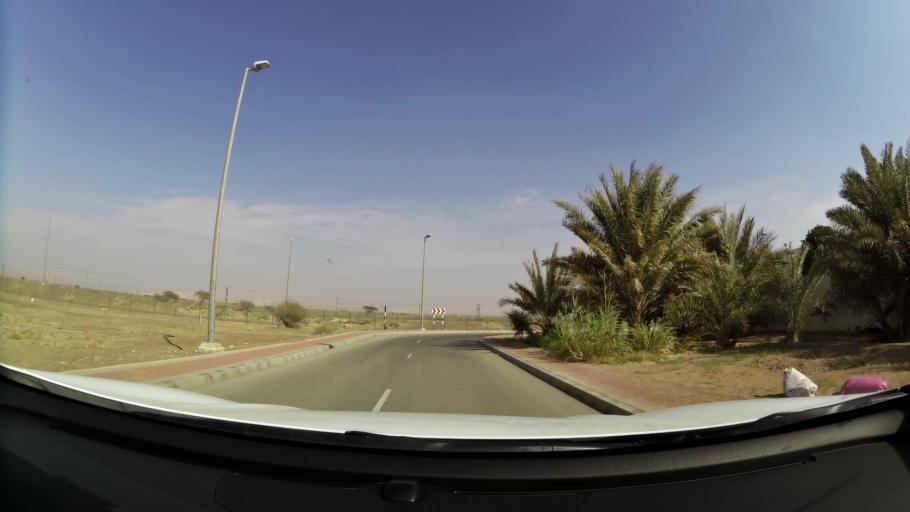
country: AE
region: Abu Dhabi
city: Al Ain
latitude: 24.0912
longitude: 55.9359
